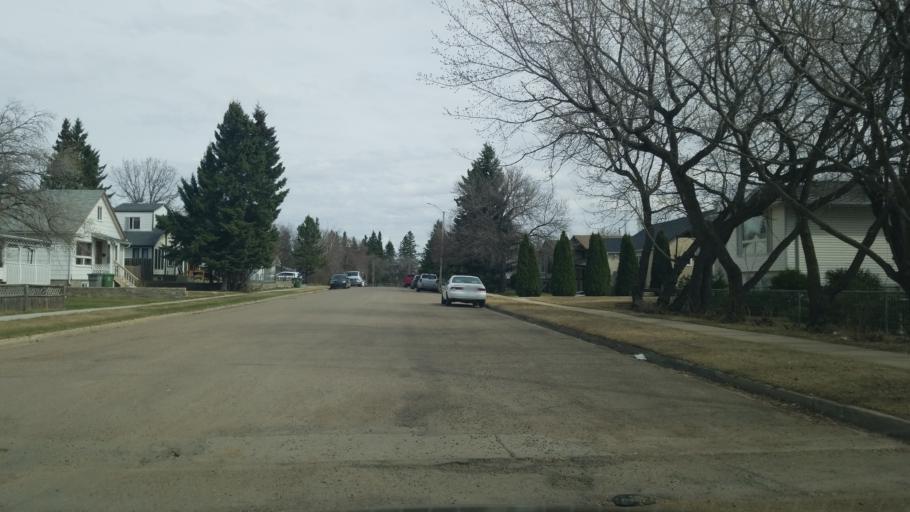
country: CA
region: Saskatchewan
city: Lloydminster
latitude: 53.2771
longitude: -110.0004
